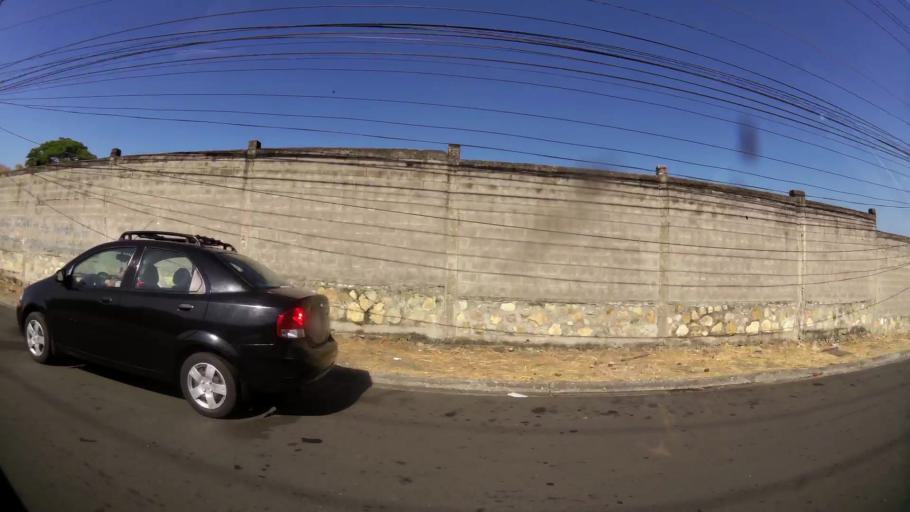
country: EC
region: Guayas
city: Eloy Alfaro
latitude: -2.1554
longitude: -79.8983
